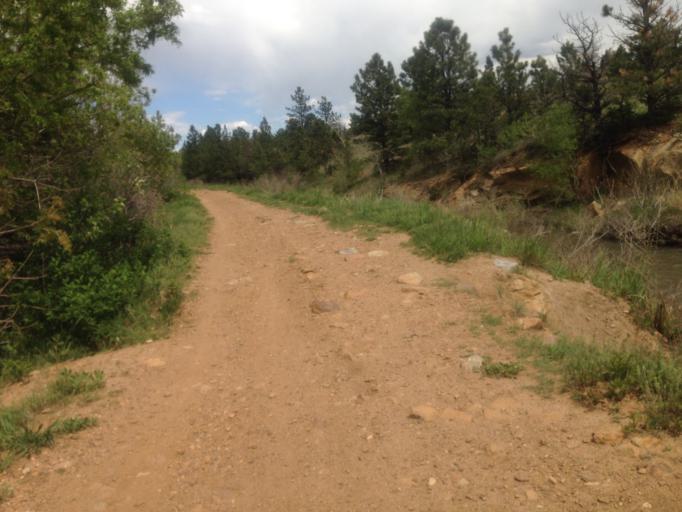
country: US
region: Colorado
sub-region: Boulder County
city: Superior
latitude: 39.9464
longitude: -105.2349
